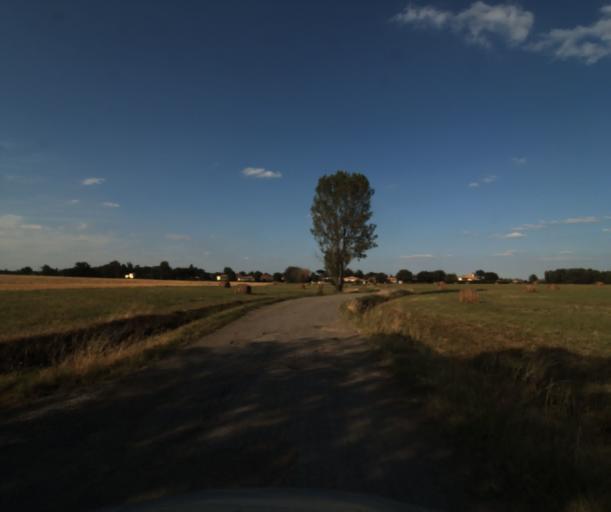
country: FR
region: Midi-Pyrenees
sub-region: Departement de la Haute-Garonne
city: Saint-Lys
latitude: 43.5012
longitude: 1.1838
